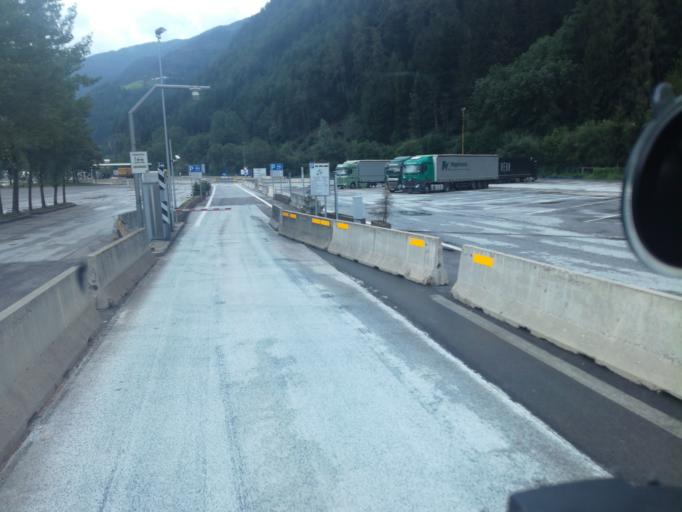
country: IT
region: Trentino-Alto Adige
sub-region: Bolzano
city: Vipiteno
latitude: 46.8821
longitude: 11.4335
